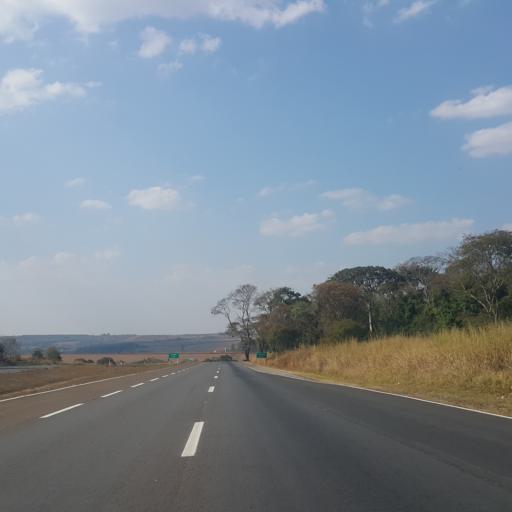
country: BR
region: Goias
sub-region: Abadiania
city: Abadiania
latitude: -16.2825
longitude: -48.7932
